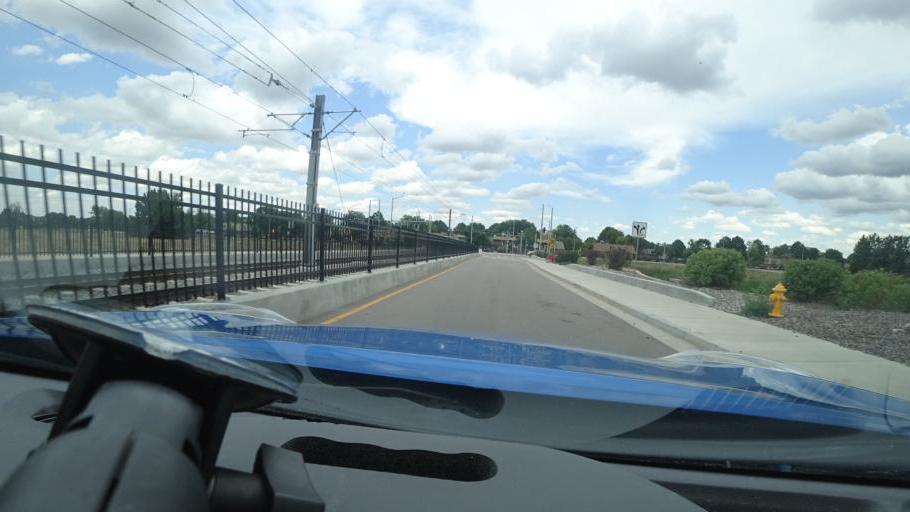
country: US
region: Colorado
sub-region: Adams County
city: Aurora
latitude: 39.7165
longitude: -104.8207
